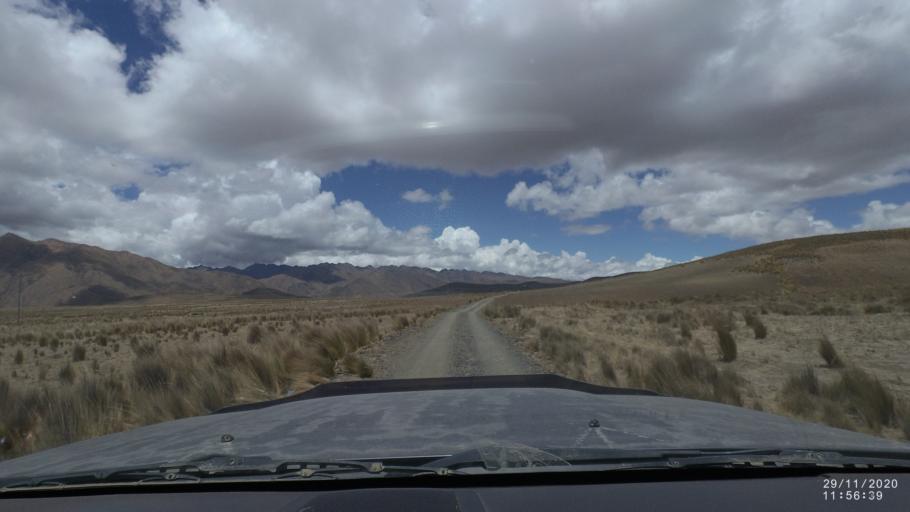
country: BO
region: Cochabamba
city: Cochabamba
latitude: -17.1630
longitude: -66.2721
